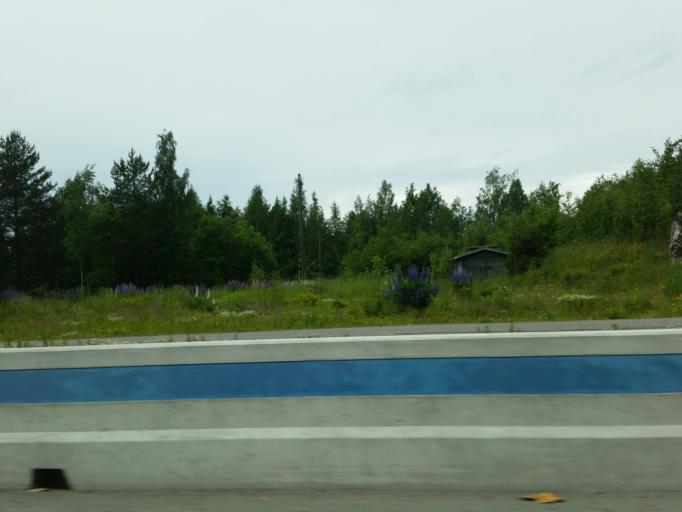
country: FI
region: Northern Savo
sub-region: Kuopio
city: Kuopio
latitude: 62.9657
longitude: 27.6990
